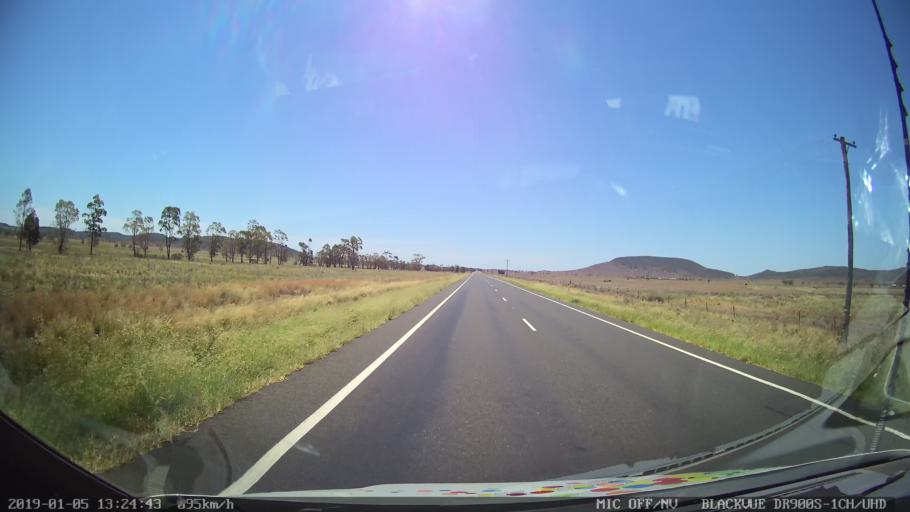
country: AU
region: New South Wales
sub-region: Gunnedah
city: Gunnedah
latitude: -31.0672
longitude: 149.9927
